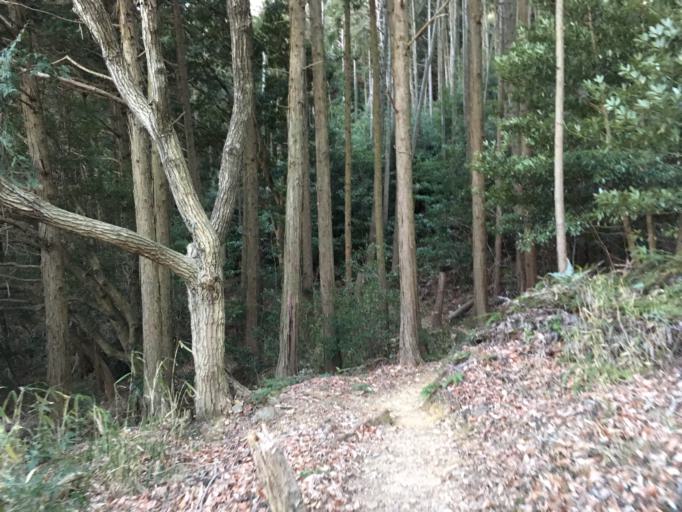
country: JP
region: Aichi
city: Toyohashi
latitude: 34.7325
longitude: 137.4450
